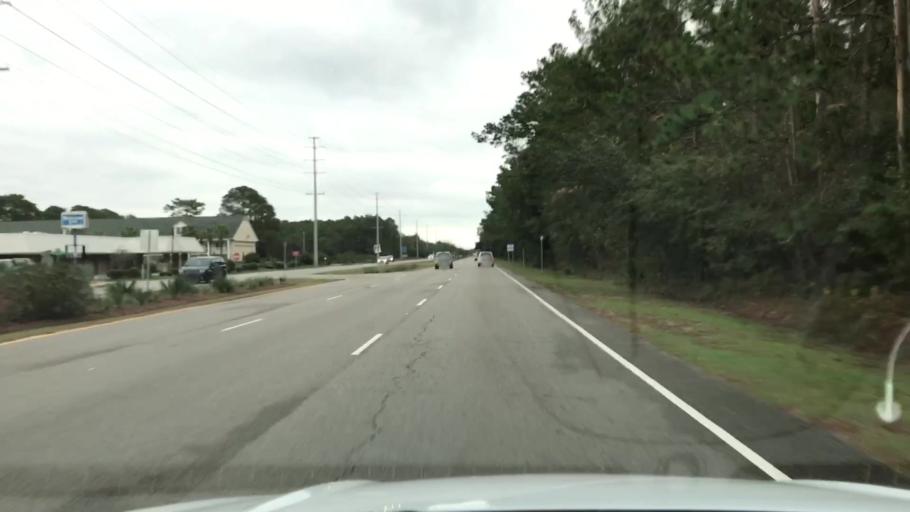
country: US
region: South Carolina
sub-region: Georgetown County
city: Georgetown
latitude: 33.4222
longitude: -79.1690
